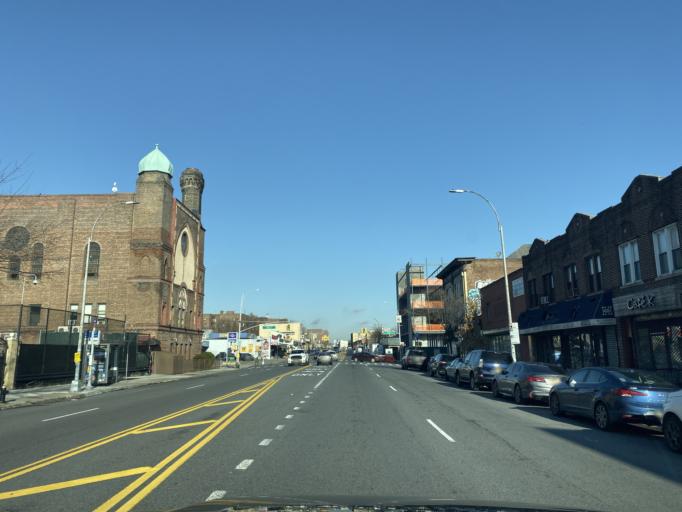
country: US
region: New York
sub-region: Kings County
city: Brooklyn
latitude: 40.6264
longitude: -73.9654
